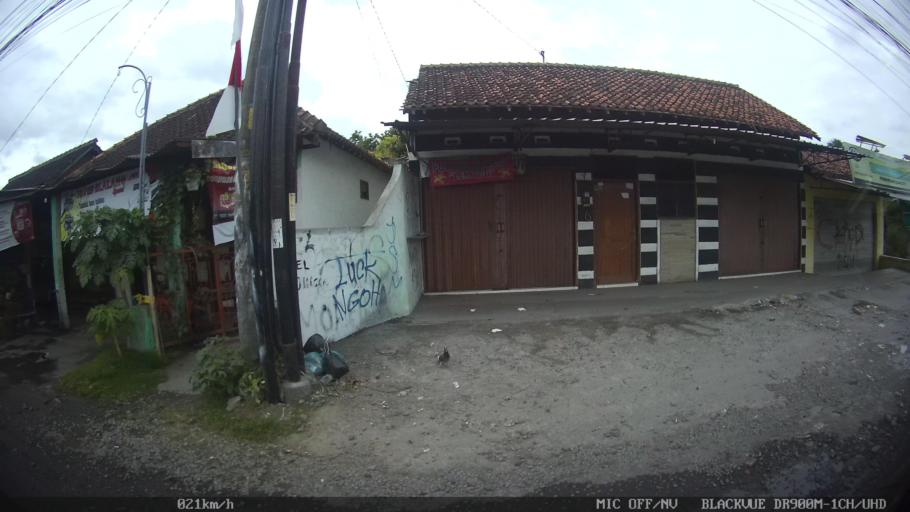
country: ID
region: Daerah Istimewa Yogyakarta
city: Yogyakarta
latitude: -7.8286
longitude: 110.4088
